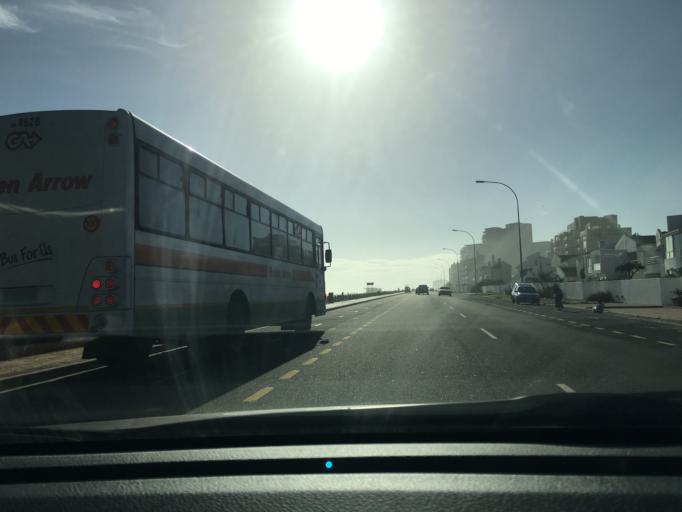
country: ZA
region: Western Cape
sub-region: City of Cape Town
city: Sunset Beach
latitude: -33.8272
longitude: 18.4802
